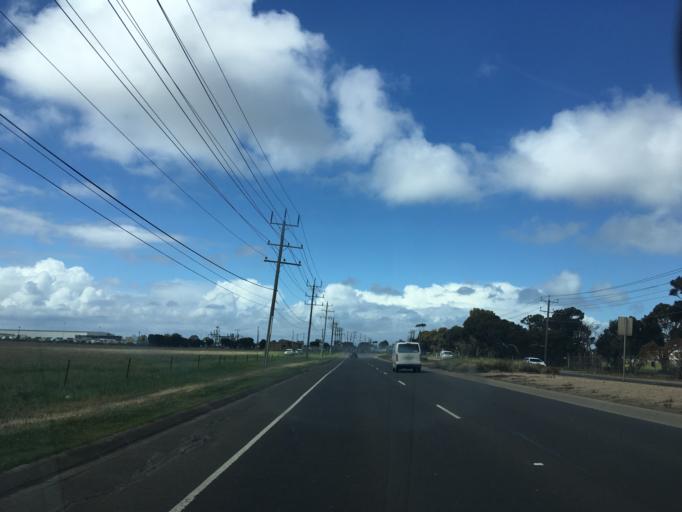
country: AU
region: Victoria
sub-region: Hobsons Bay
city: Laverton
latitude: -37.8456
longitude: 144.7971
